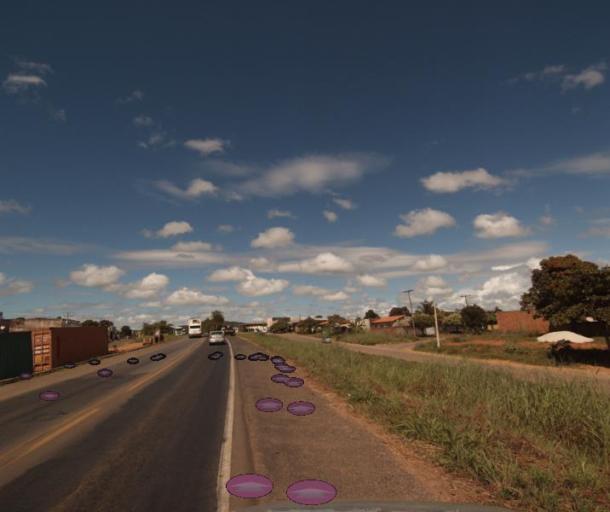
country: BR
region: Goias
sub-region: Uruacu
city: Uruacu
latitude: -14.5244
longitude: -49.1589
